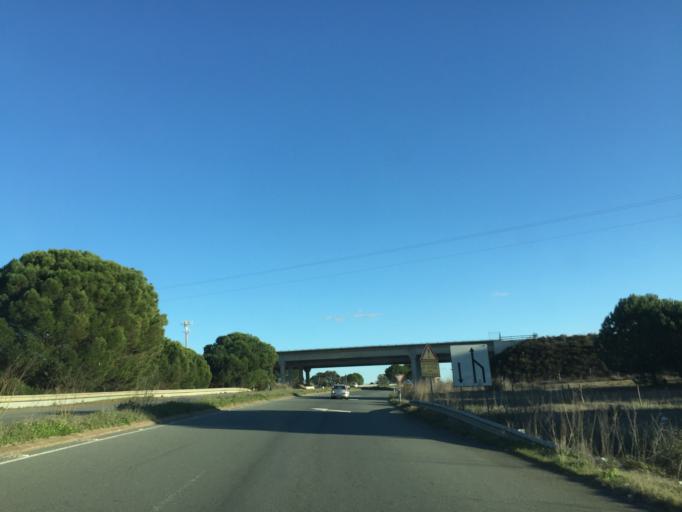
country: PT
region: Setubal
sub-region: Grandola
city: Grandola
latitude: 38.1178
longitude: -8.4211
